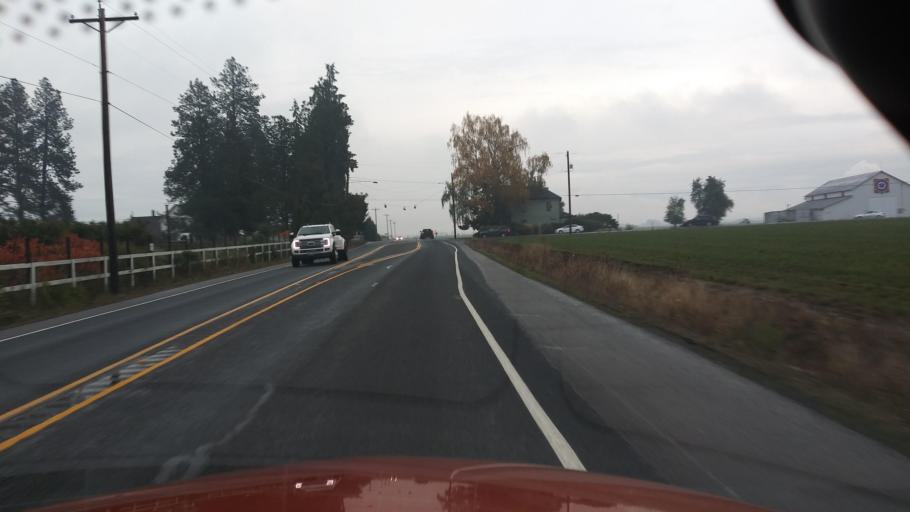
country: US
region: Oregon
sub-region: Washington County
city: North Plains
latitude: 45.5727
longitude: -123.0374
